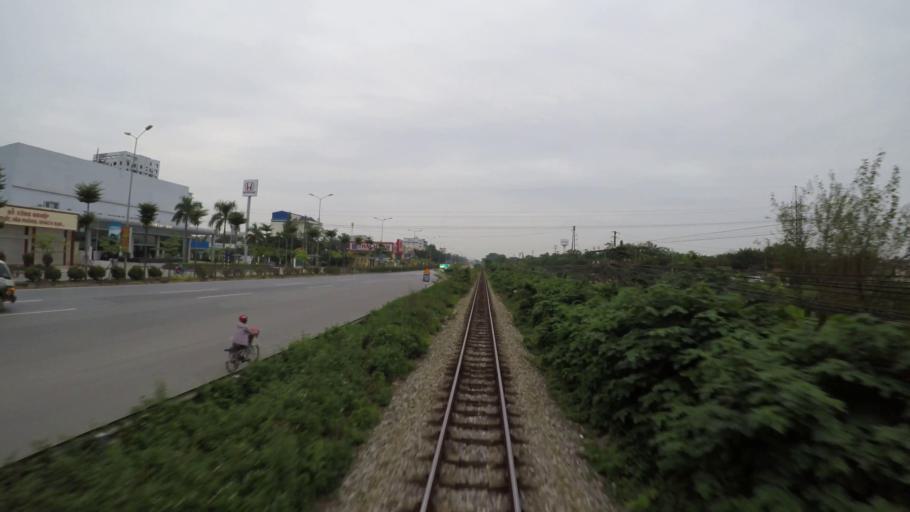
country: VN
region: Ha Noi
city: Trau Quy
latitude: 21.0060
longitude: 105.9590
